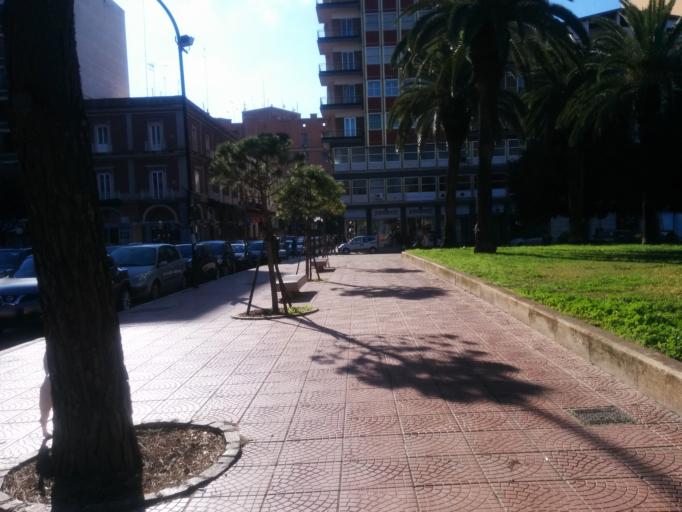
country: IT
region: Apulia
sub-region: Provincia di Taranto
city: Taranto
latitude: 40.4726
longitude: 17.2384
